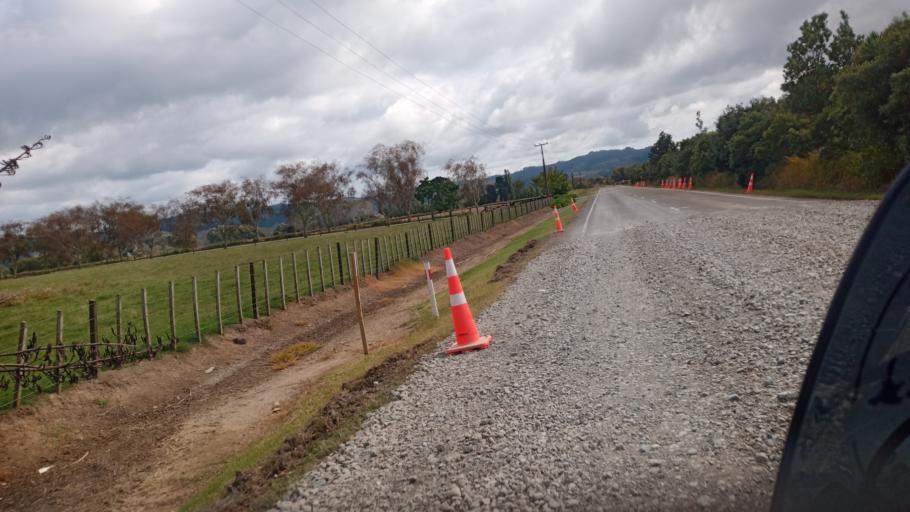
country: NZ
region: Gisborne
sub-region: Gisborne District
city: Gisborne
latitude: -38.3456
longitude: 178.2985
